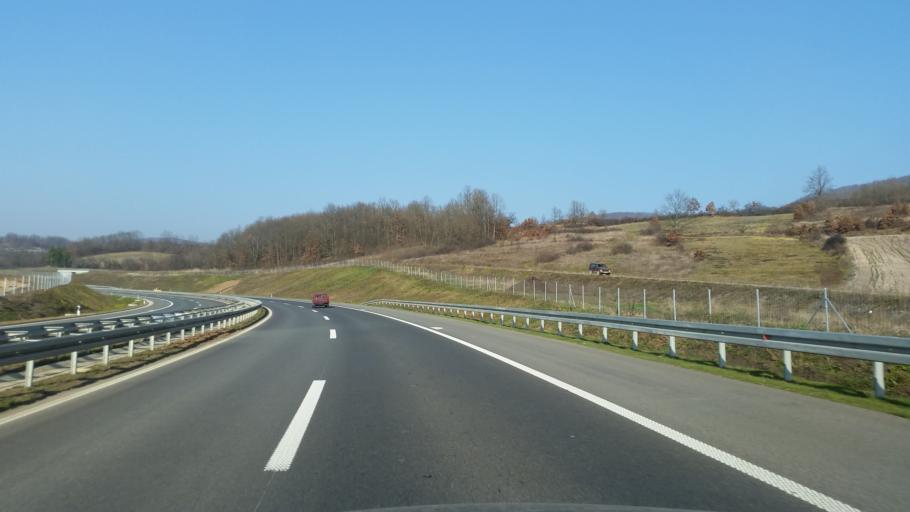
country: RS
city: Prislonica
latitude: 43.9981
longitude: 20.4035
